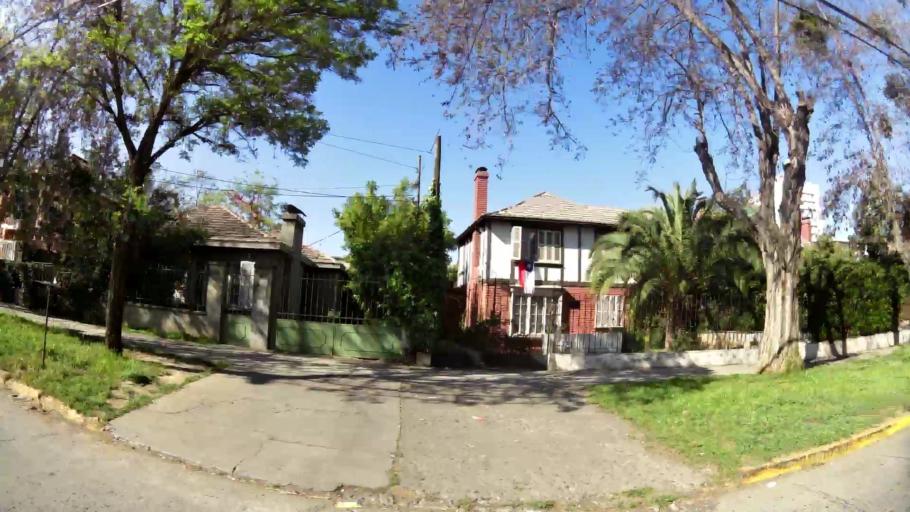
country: CL
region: Santiago Metropolitan
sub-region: Provincia de Santiago
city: Villa Presidente Frei, Nunoa, Santiago, Chile
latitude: -33.4518
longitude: -70.5723
